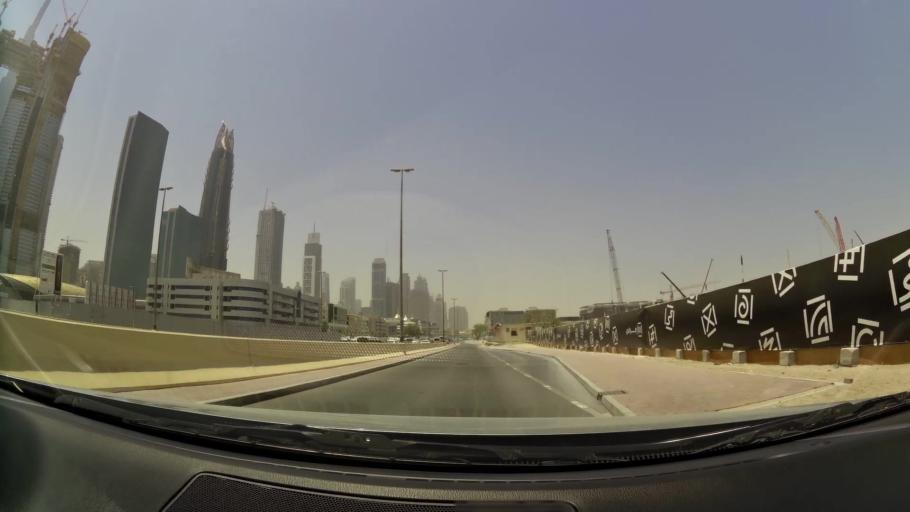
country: AE
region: Dubai
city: Dubai
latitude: 25.2047
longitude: 55.2679
